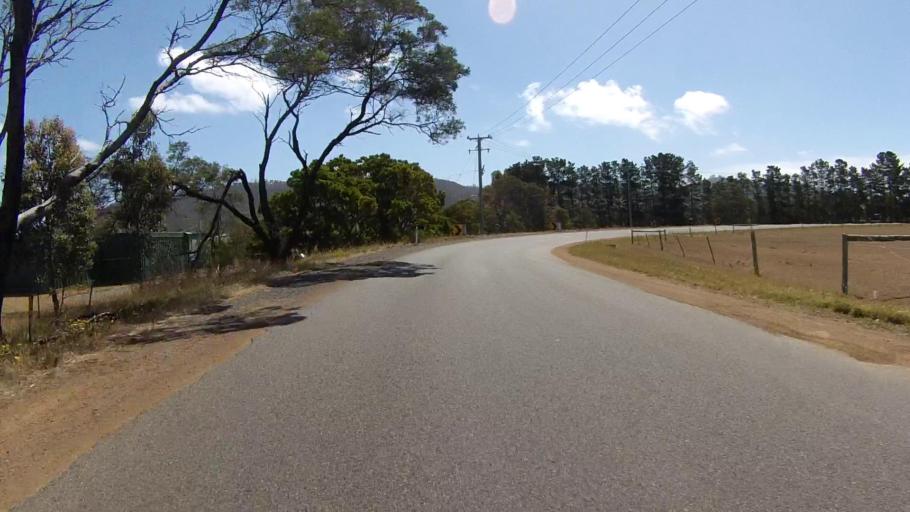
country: AU
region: Tasmania
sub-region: Clarence
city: Acton Park
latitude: -42.8928
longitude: 147.4957
